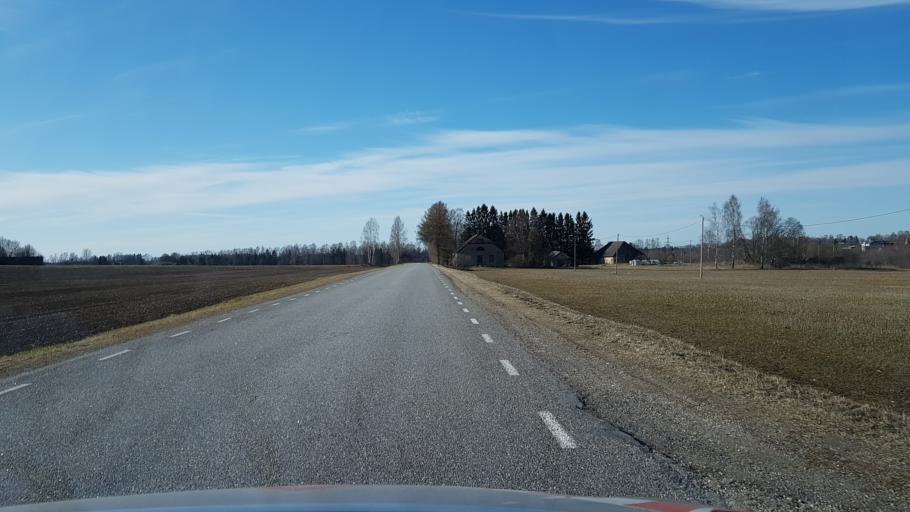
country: EE
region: Laeaene-Virumaa
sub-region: Kadrina vald
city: Kadrina
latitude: 59.3317
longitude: 26.1323
